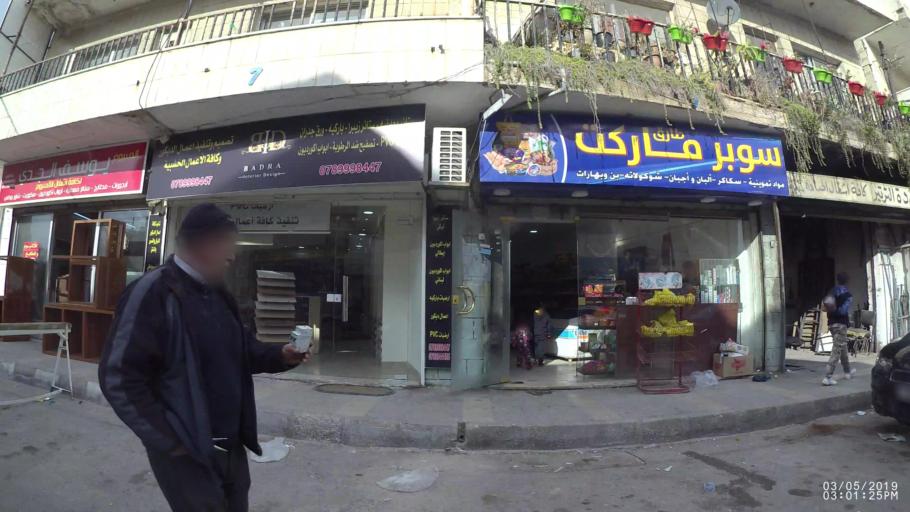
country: JO
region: Amman
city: Amman
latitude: 31.9992
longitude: 35.9454
